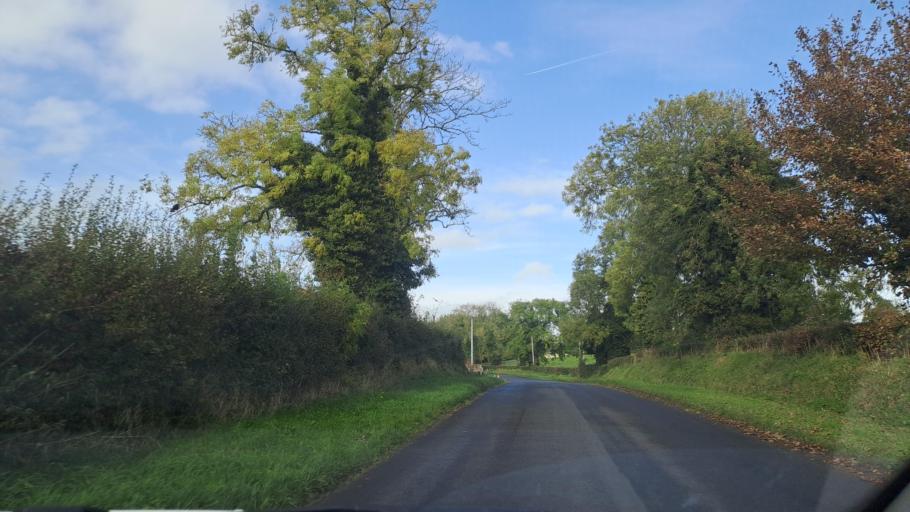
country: IE
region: Leinster
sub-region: Lu
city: Ardee
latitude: 53.8574
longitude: -6.6573
